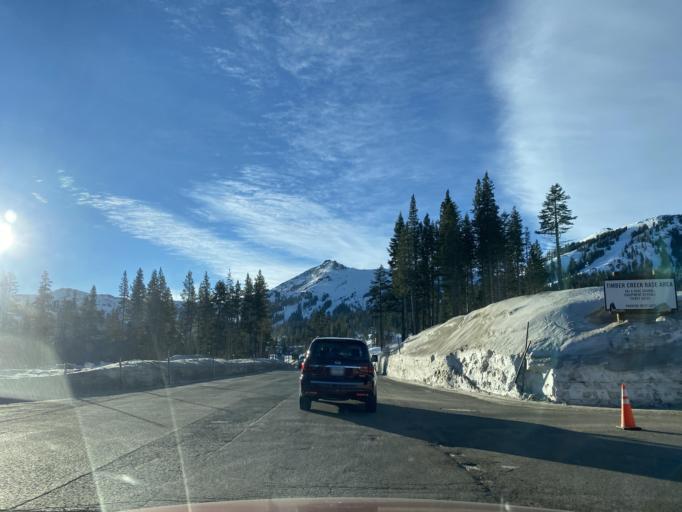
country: US
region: California
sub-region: El Dorado County
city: South Lake Tahoe
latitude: 38.6907
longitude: -120.0744
